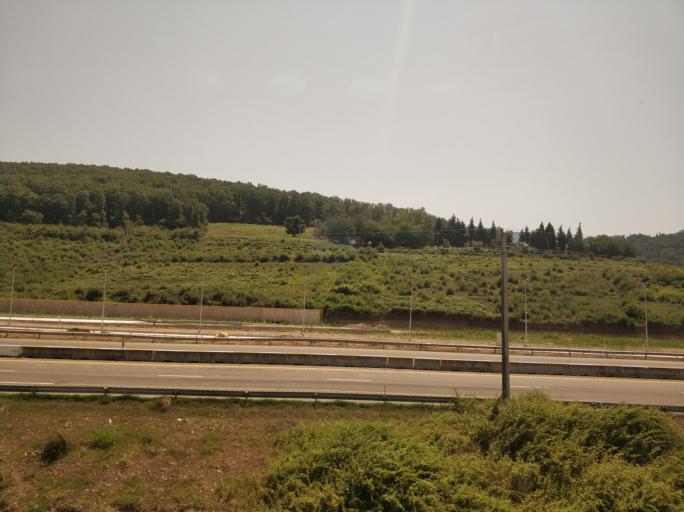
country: IR
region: Gilan
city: Pa'in-e Bazar-e Rudbar
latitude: 36.9428
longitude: 49.5488
